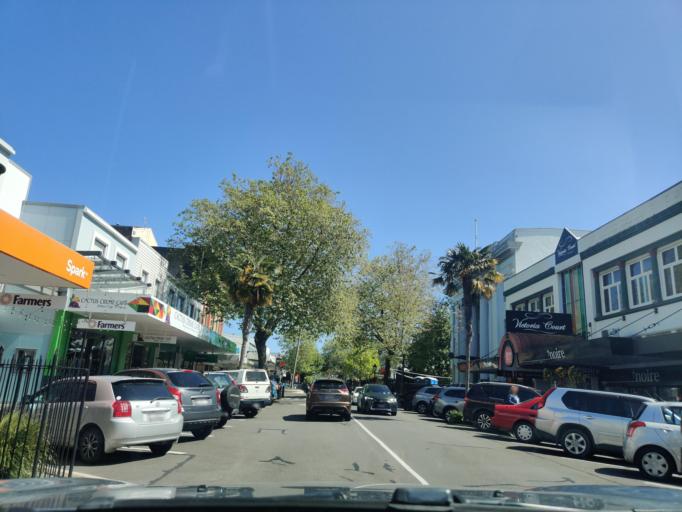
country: NZ
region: Manawatu-Wanganui
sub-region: Wanganui District
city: Wanganui
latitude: -39.9332
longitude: 175.0525
